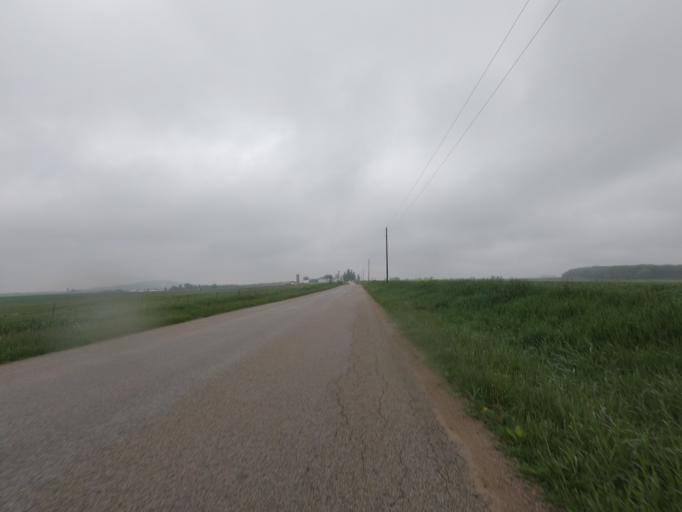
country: US
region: Wisconsin
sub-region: Grant County
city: Hazel Green
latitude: 42.5014
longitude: -90.5081
